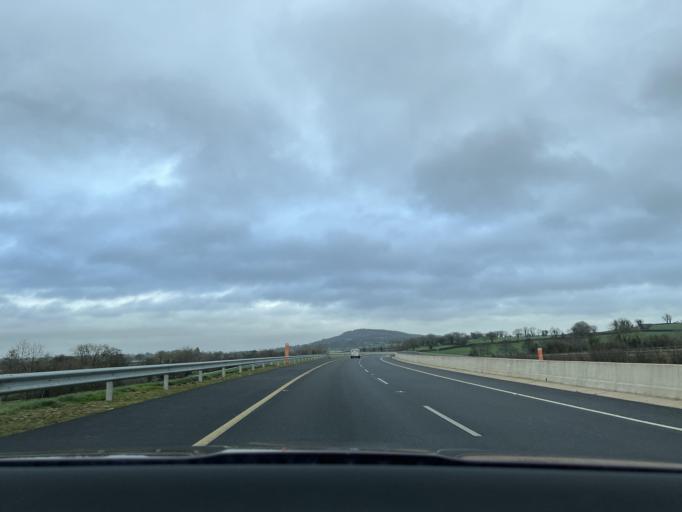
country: IE
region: Leinster
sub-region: Loch Garman
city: Ferns
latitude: 52.5728
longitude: -6.4407
